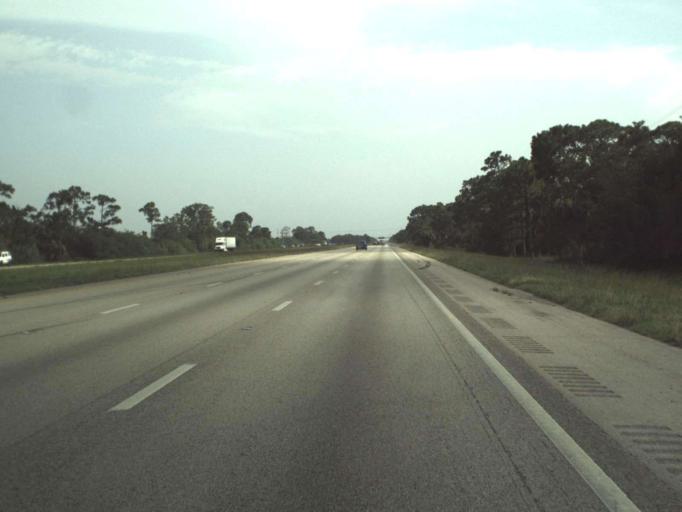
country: US
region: Florida
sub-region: Saint Lucie County
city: River Park
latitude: 27.3446
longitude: -80.4144
